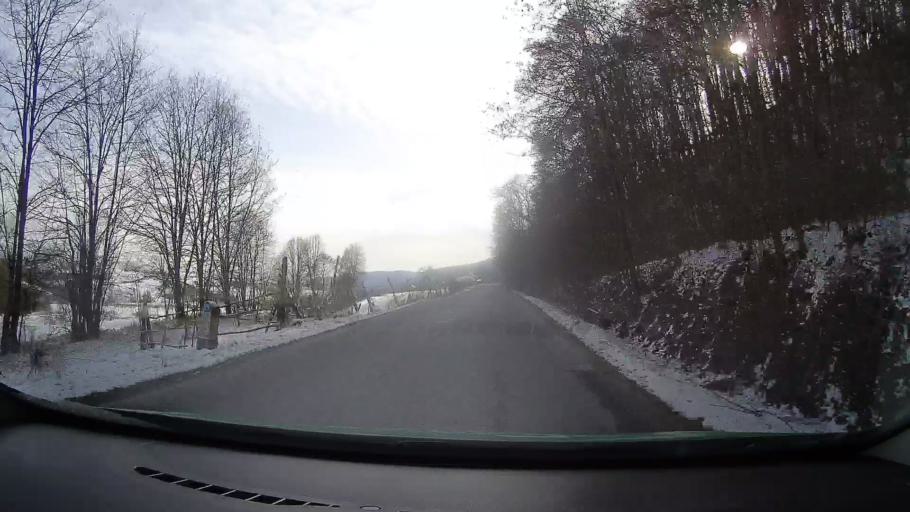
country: RO
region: Mures
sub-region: Comuna Apold
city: Saes
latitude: 46.1775
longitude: 24.7574
